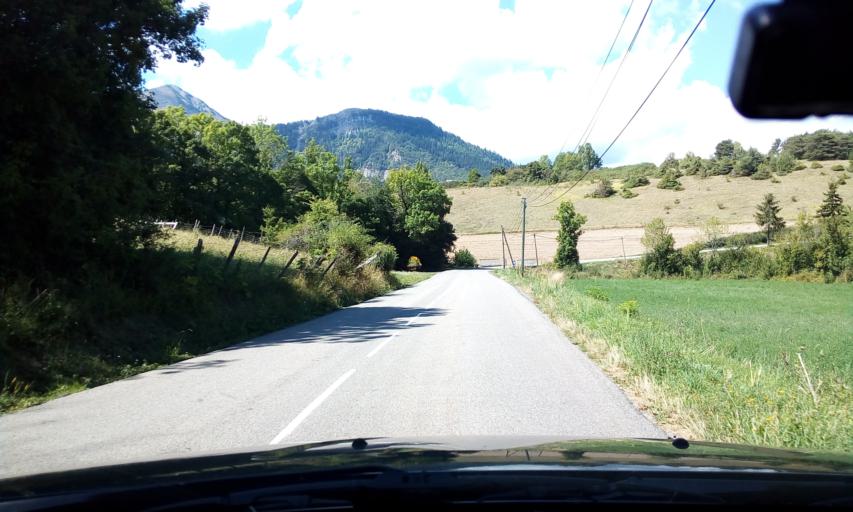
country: FR
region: Rhone-Alpes
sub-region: Departement de l'Isere
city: Mens
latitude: 44.7595
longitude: 5.6711
